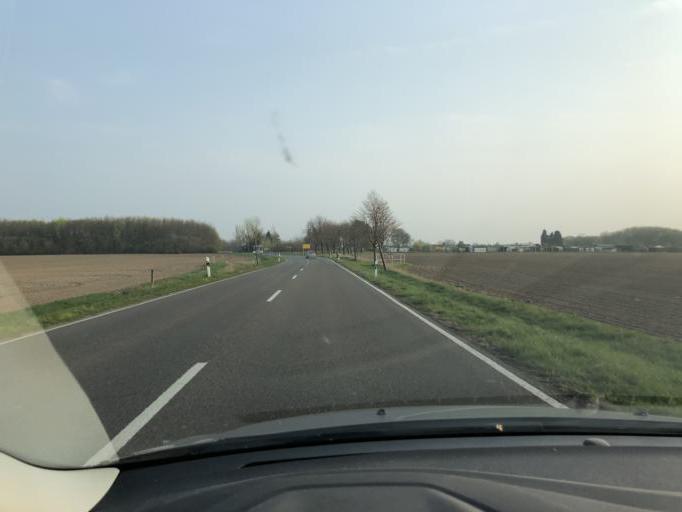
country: DE
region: Saxony
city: Zschortau
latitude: 51.4683
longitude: 12.3474
